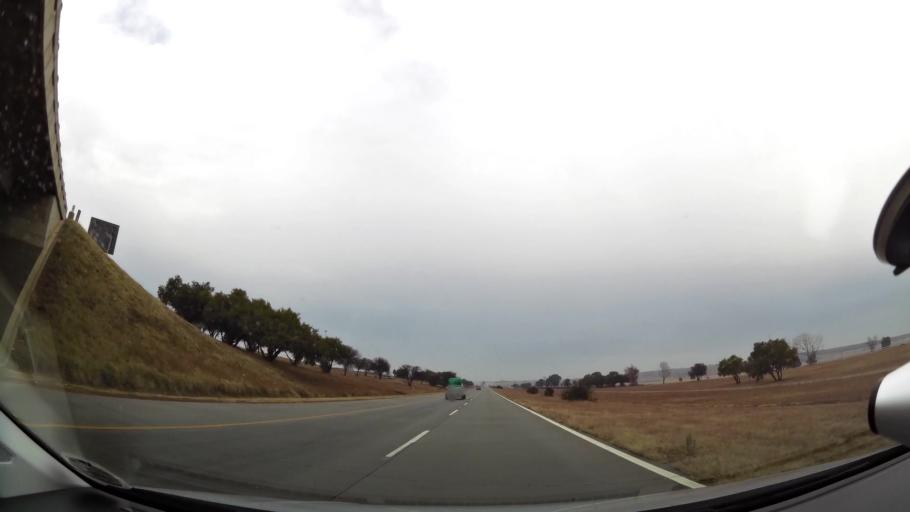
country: ZA
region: Gauteng
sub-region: City of Johannesburg Metropolitan Municipality
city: Orange Farm
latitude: -26.5340
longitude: 27.8082
